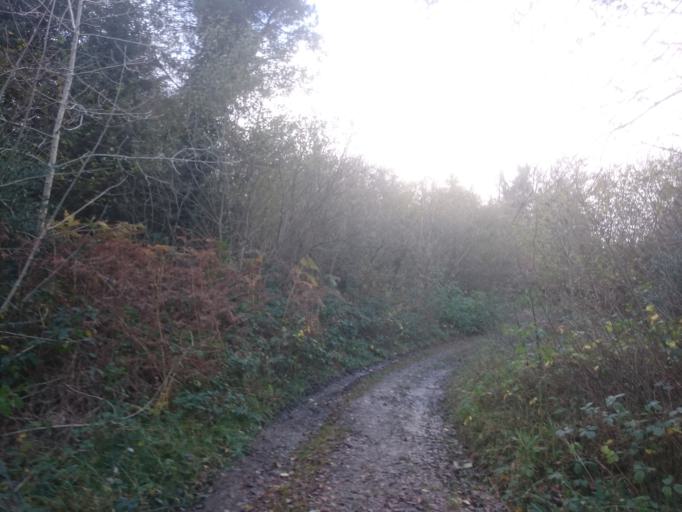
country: IE
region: Leinster
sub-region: Kilkenny
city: Thomastown
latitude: 52.4631
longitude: -7.0560
